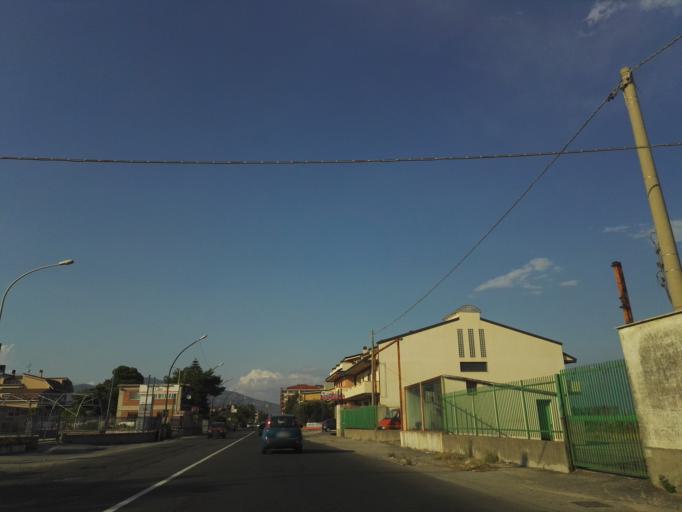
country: IT
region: Calabria
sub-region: Provincia di Reggio Calabria
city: Siderno
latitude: 38.2821
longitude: 16.3116
